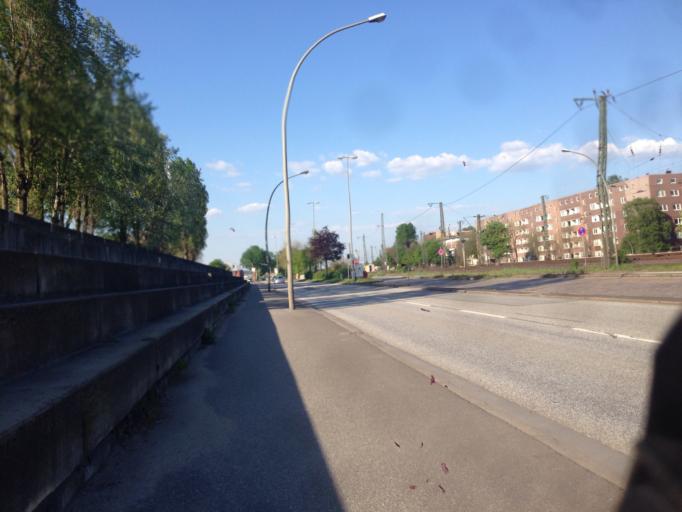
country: DE
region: Hamburg
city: Kleiner Grasbrook
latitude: 53.5257
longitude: 10.0152
